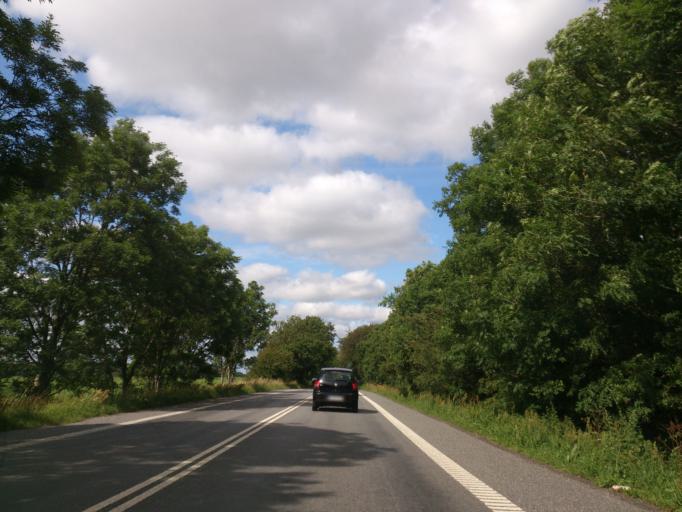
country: DK
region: South Denmark
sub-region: Aabenraa Kommune
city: Krusa
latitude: 54.9097
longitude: 9.4414
